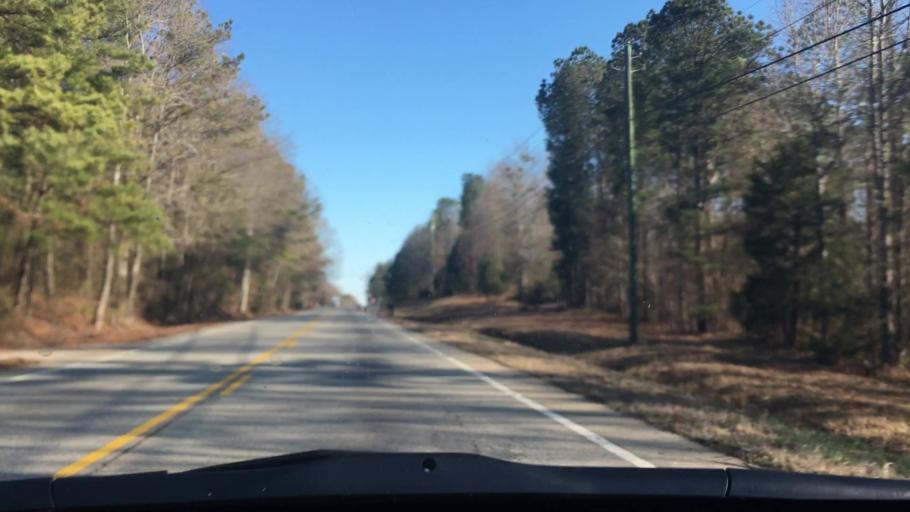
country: US
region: Georgia
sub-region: Henry County
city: McDonough
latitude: 33.4918
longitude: -84.0854
